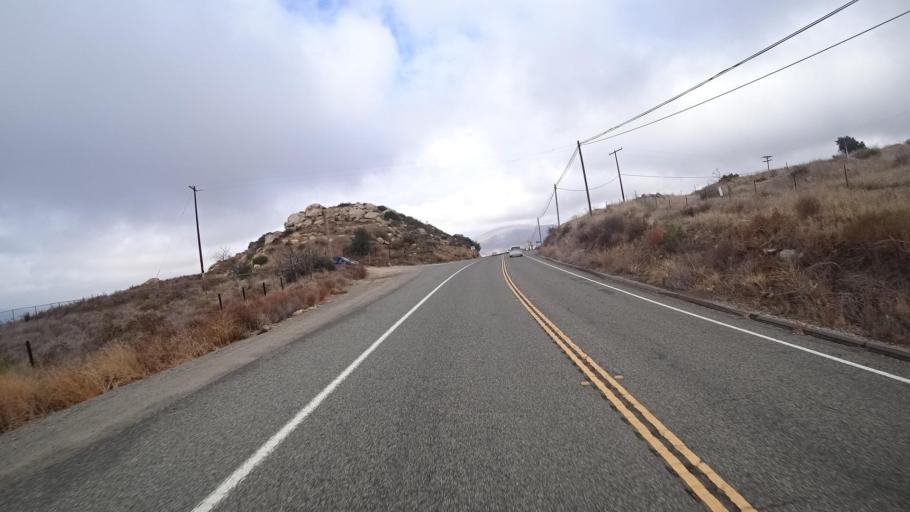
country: MX
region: Baja California
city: Tecate
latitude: 32.6005
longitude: -116.5915
